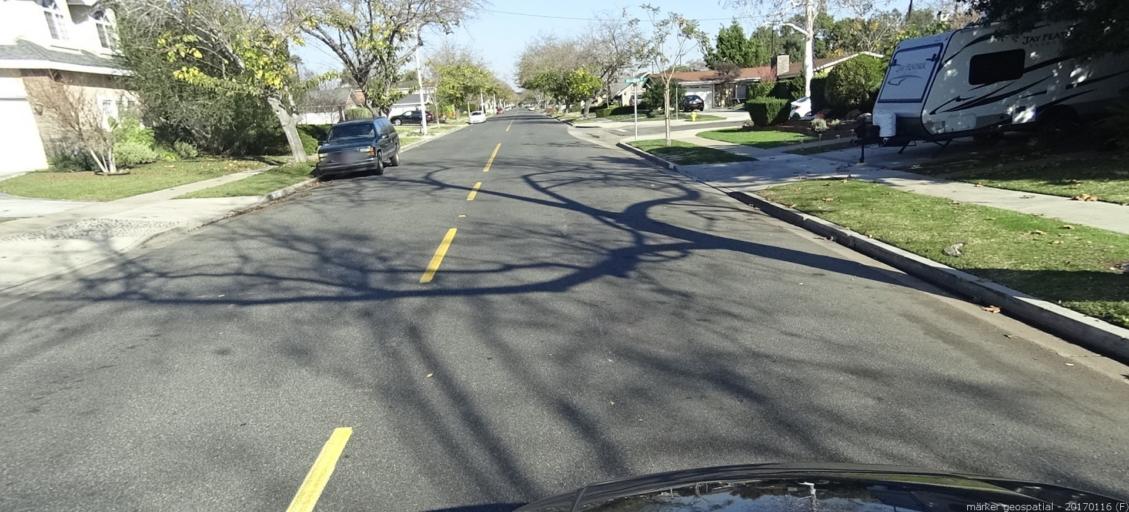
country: US
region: California
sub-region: Orange County
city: Rossmoor
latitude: 33.7804
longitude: -118.0819
